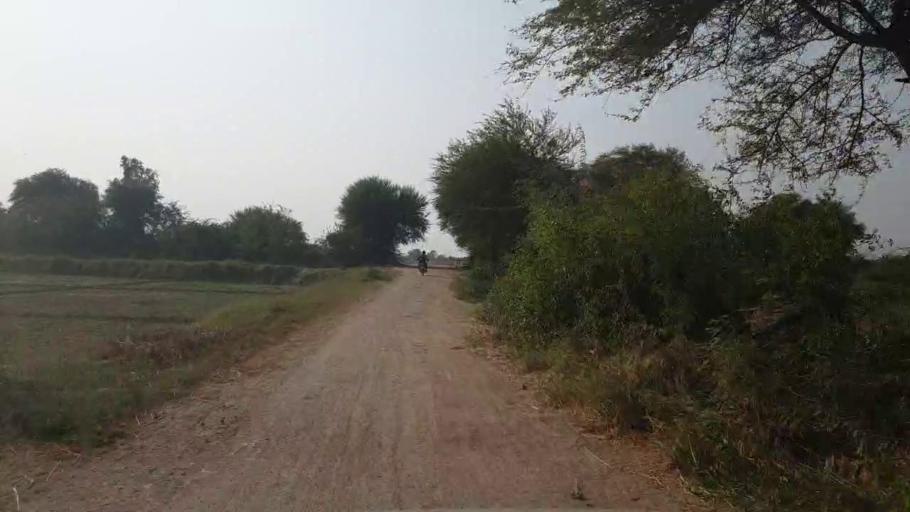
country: PK
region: Sindh
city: Bulri
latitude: 25.0460
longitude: 68.3690
